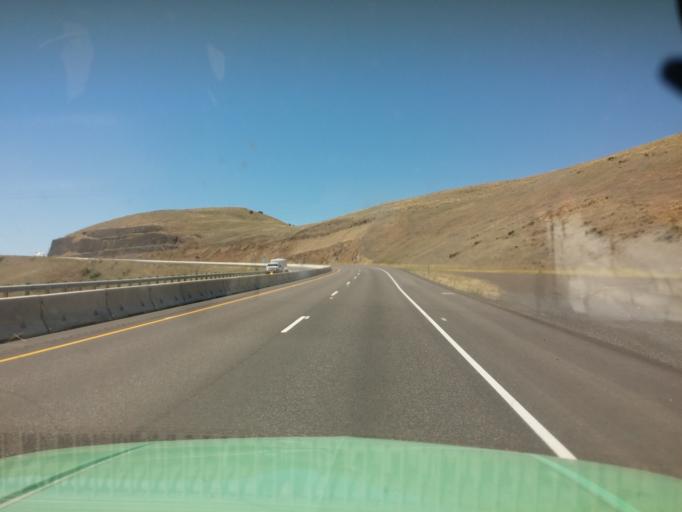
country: US
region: Idaho
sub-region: Nez Perce County
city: Lewiston
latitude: 46.4622
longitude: -116.9813
